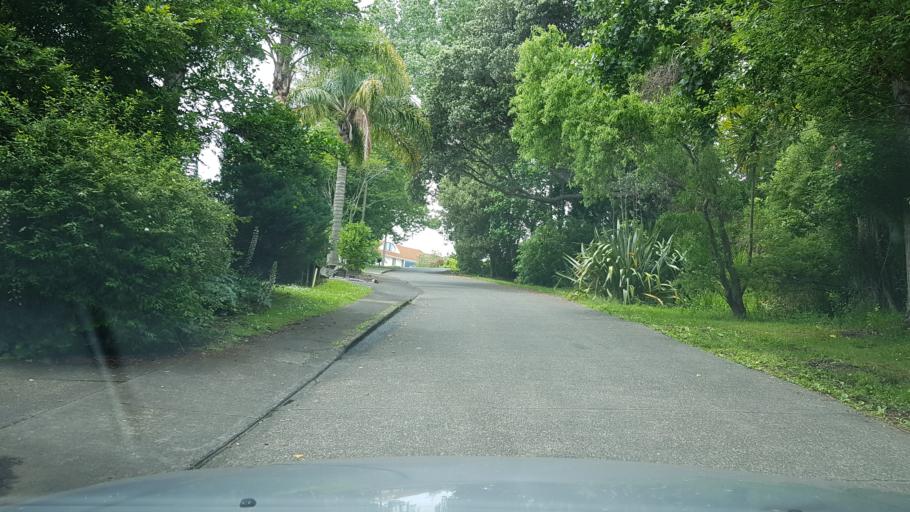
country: NZ
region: Auckland
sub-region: Auckland
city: North Shore
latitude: -36.8173
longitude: 174.7289
